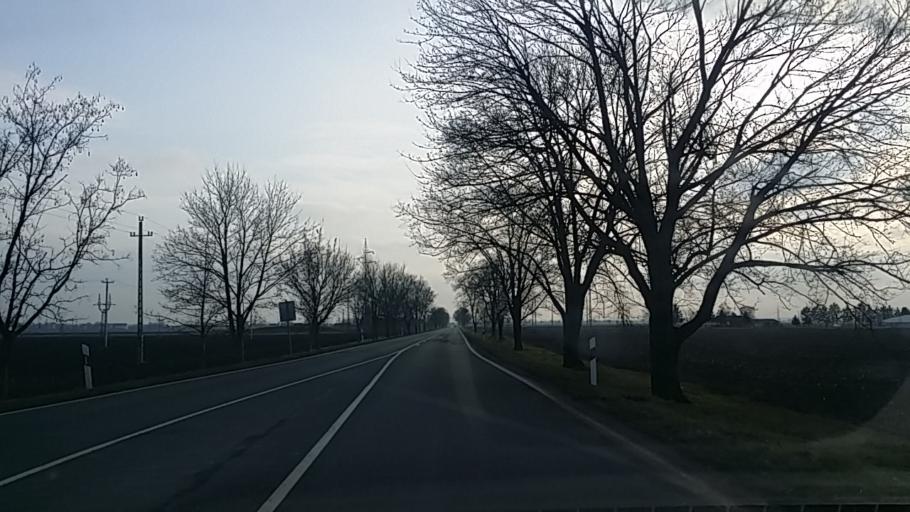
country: HU
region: Baranya
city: Lanycsok
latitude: 46.0164
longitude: 18.6566
